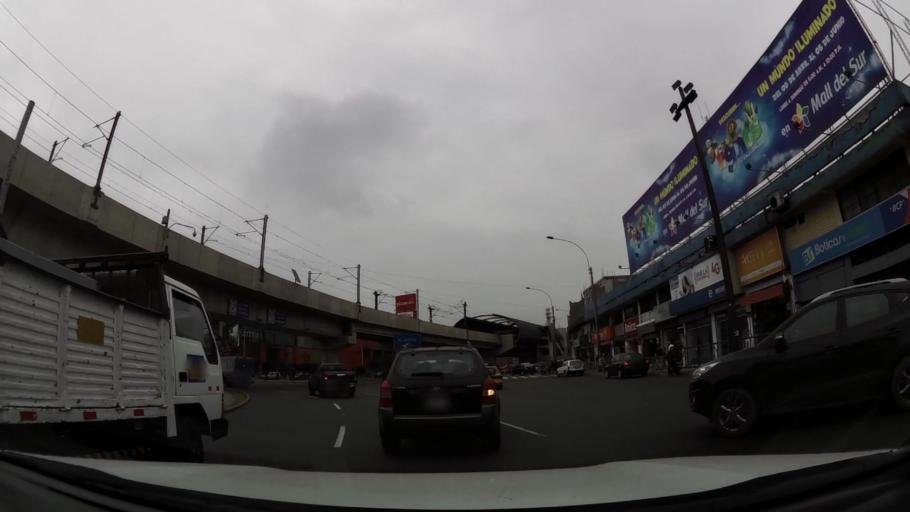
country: PE
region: Lima
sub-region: Lima
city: Surco
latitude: -12.1288
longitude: -77.0006
